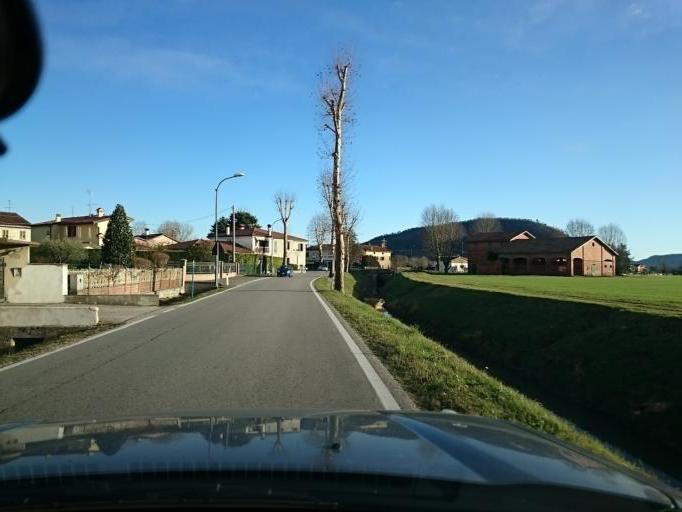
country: IT
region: Veneto
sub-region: Provincia di Padova
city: San Biagio
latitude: 45.3658
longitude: 11.7429
